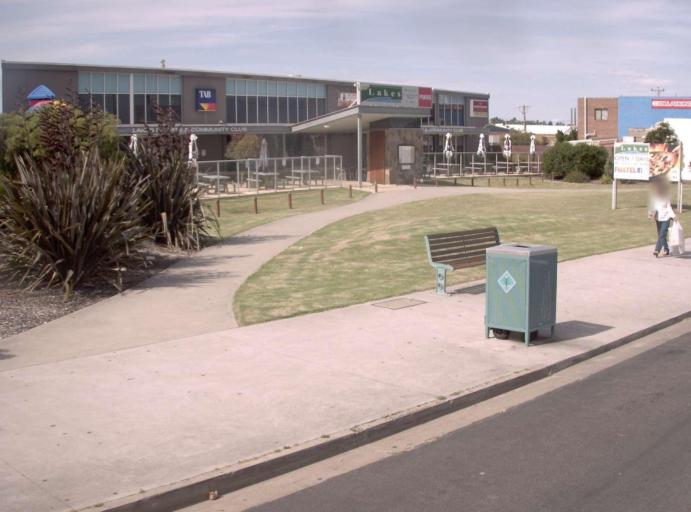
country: AU
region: Victoria
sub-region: East Gippsland
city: Lakes Entrance
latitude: -37.8801
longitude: 147.9896
